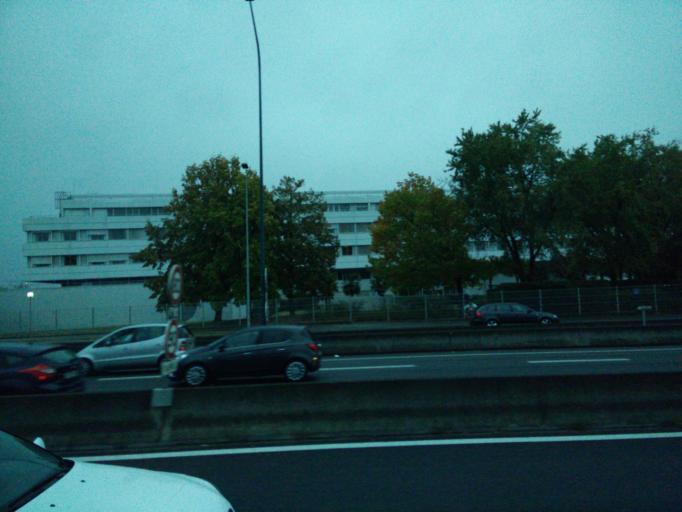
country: FR
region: Midi-Pyrenees
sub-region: Departement de la Haute-Garonne
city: Blagnac
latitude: 43.6246
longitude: 1.3866
